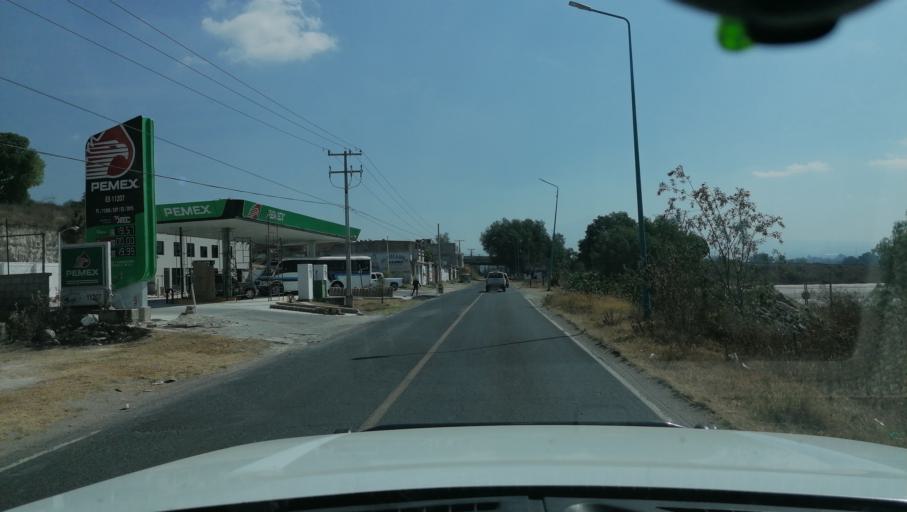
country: MX
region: Tlaxcala
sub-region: Tetlatlahuca
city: Santa Cruz Aquiahuac
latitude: 19.2375
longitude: -98.2772
